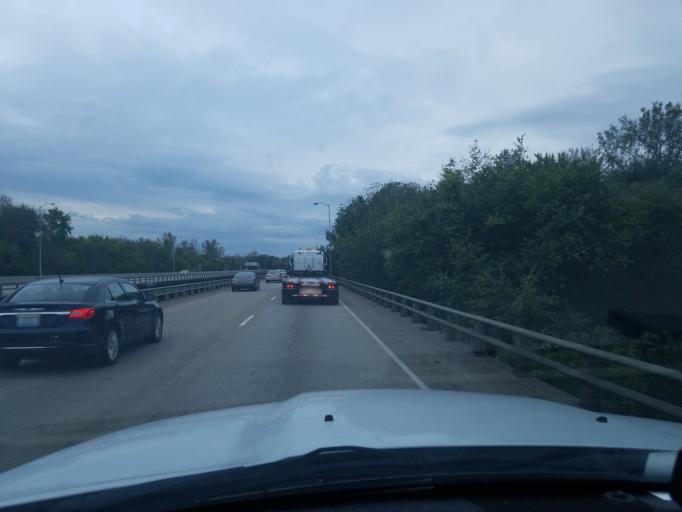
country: US
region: Indiana
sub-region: Vanderburgh County
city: Evansville
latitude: 37.9382
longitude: -87.5454
